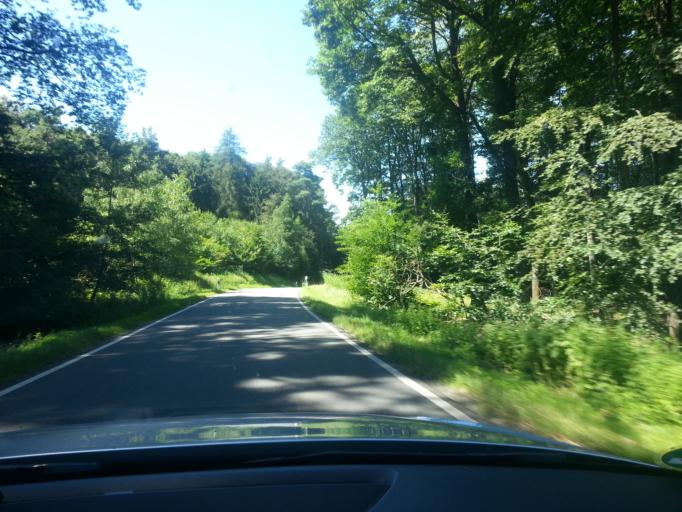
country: DE
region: Rheinland-Pfalz
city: Fockelberg
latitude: 49.5328
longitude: 7.4857
